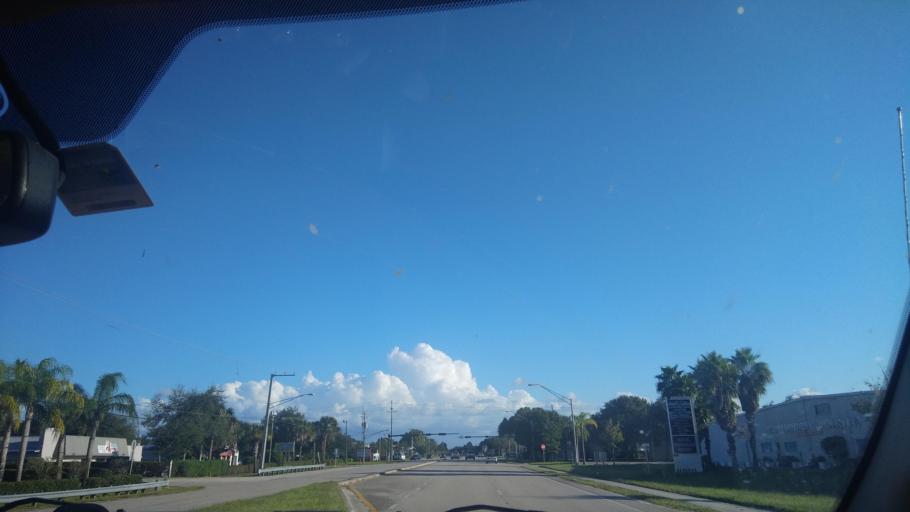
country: US
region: Florida
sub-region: Indian River County
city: Gifford
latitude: 27.6764
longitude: -80.4091
